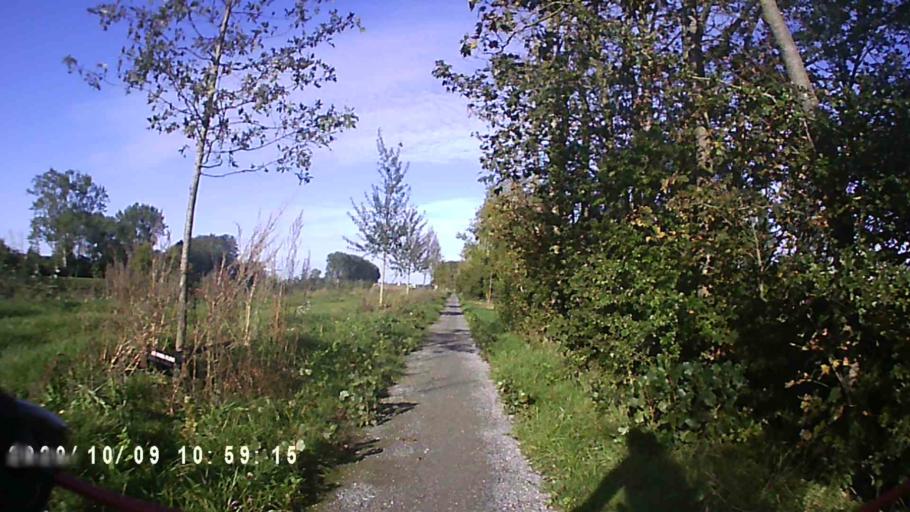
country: NL
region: Groningen
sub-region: Gemeente Zuidhorn
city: Aduard
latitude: 53.2560
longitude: 6.5140
